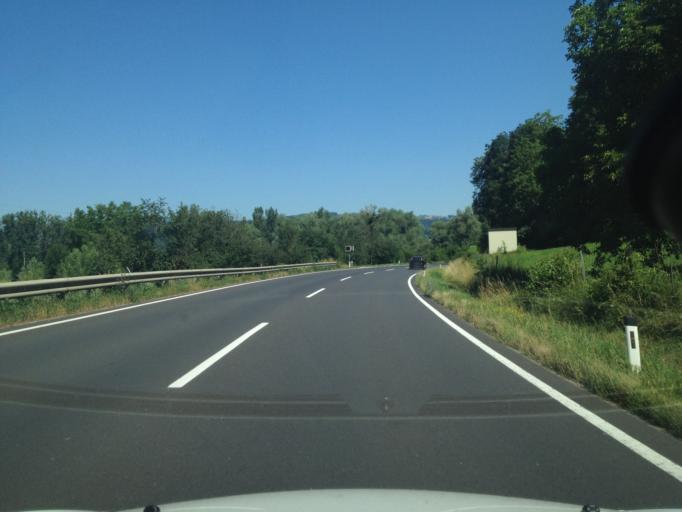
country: AT
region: Upper Austria
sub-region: Politischer Bezirk Urfahr-Umgebung
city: Steyregg
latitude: 48.3118
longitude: 14.3353
